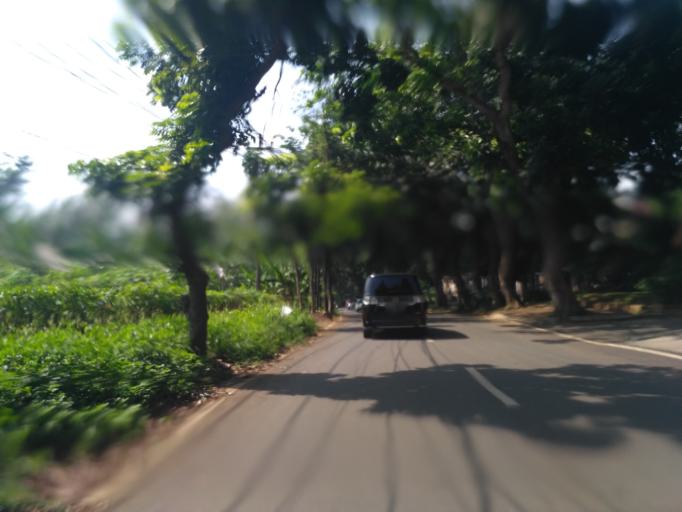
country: ID
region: Central Java
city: Semarang
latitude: -7.0246
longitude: 110.4142
